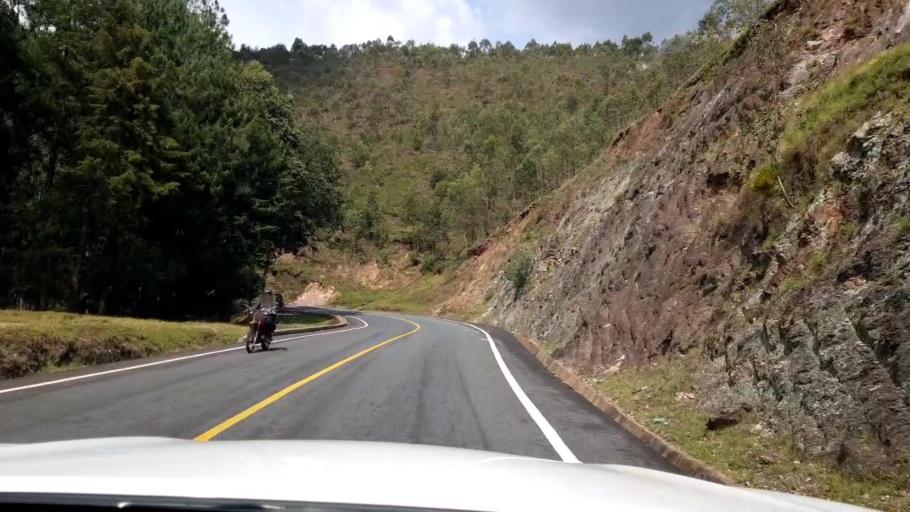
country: RW
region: Southern Province
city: Gitarama
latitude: -2.0303
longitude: 29.7171
